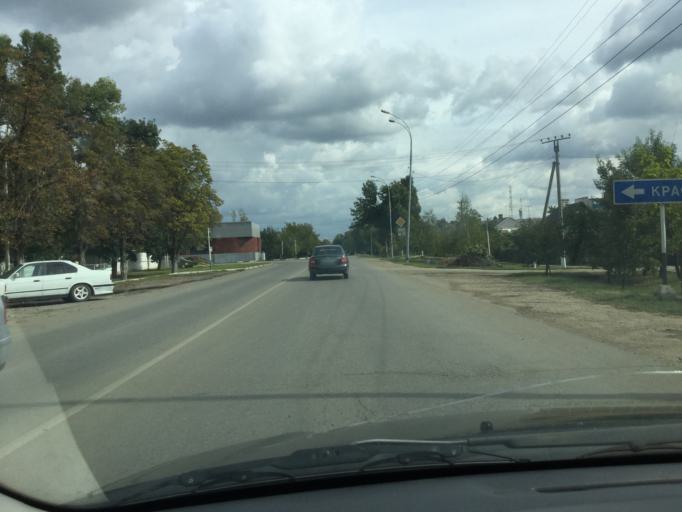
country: RU
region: Krasnodarskiy
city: Slavyansk-na-Kubani
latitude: 45.2518
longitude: 38.1065
